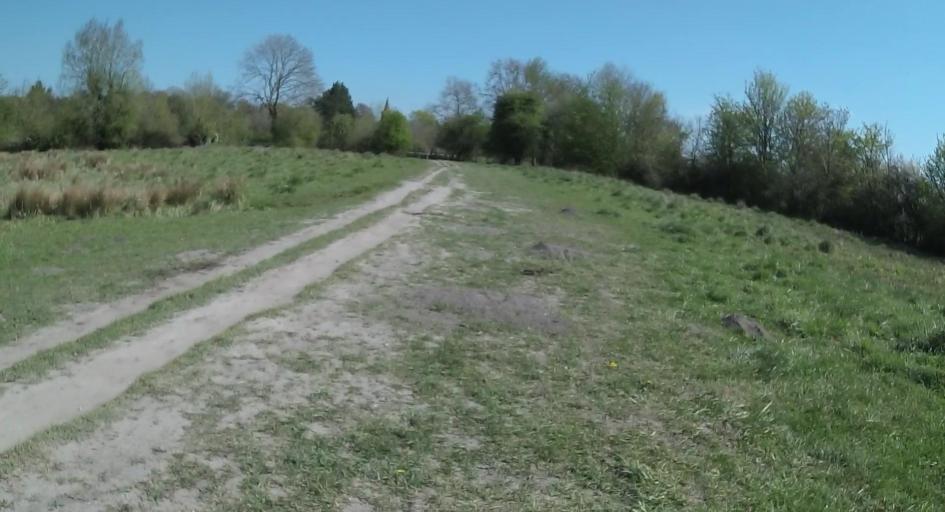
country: GB
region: England
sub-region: Hampshire
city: Compton
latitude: 51.0257
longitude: -1.3213
